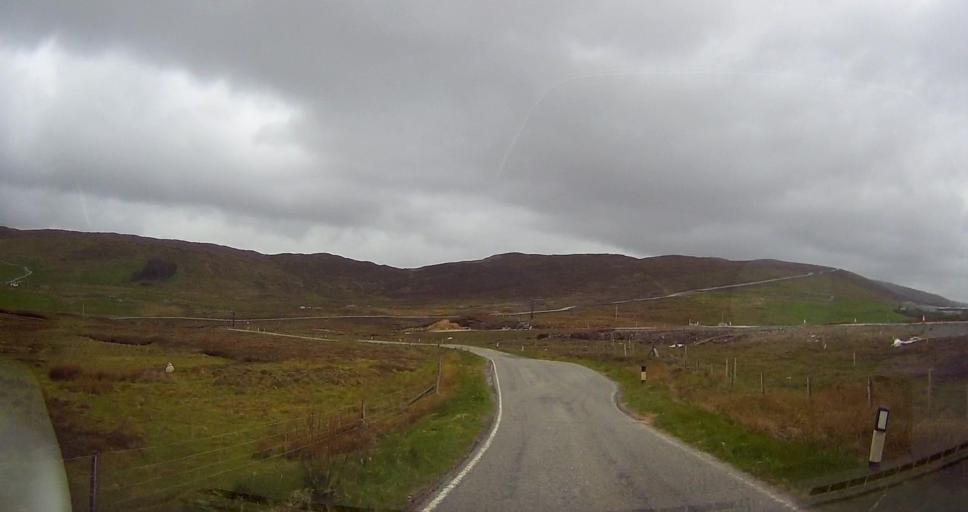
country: GB
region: Scotland
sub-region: Shetland Islands
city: Lerwick
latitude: 60.2776
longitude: -1.2654
